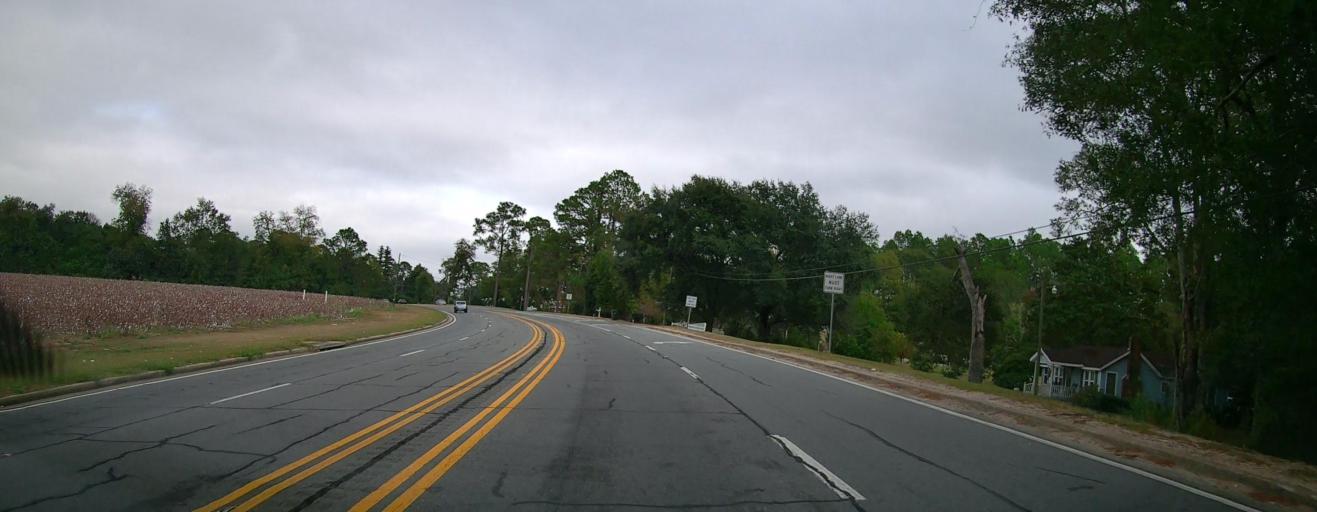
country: US
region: Georgia
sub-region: Tift County
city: Omega
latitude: 31.2642
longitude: -83.6898
